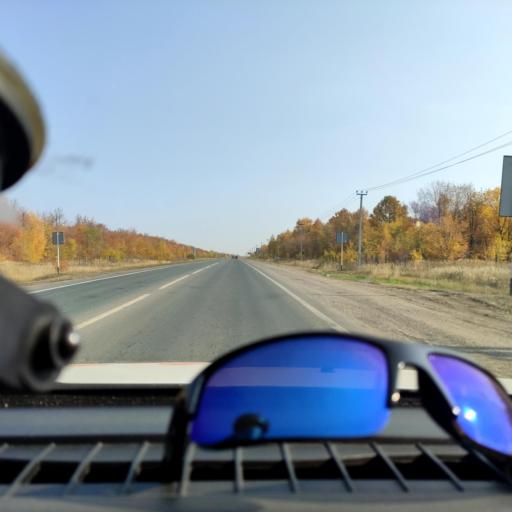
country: RU
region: Samara
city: Chapayevsk
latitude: 52.9964
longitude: 49.7911
